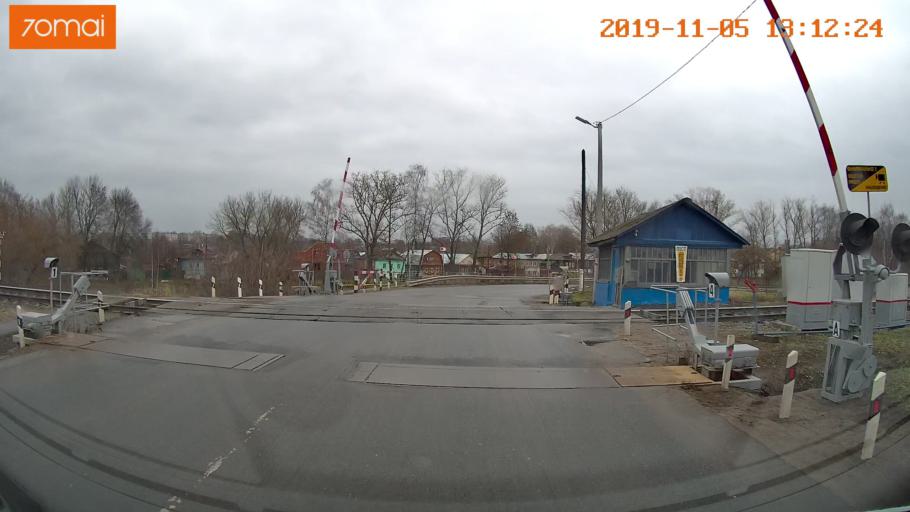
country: RU
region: Ivanovo
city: Shuya
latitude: 56.8569
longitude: 41.3511
